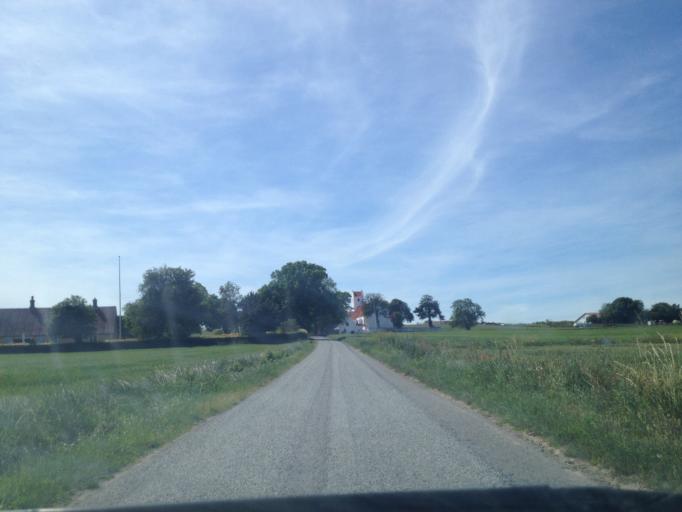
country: DK
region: Central Jutland
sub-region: Samso Kommune
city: Tranebjerg
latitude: 55.9511
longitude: 10.5513
